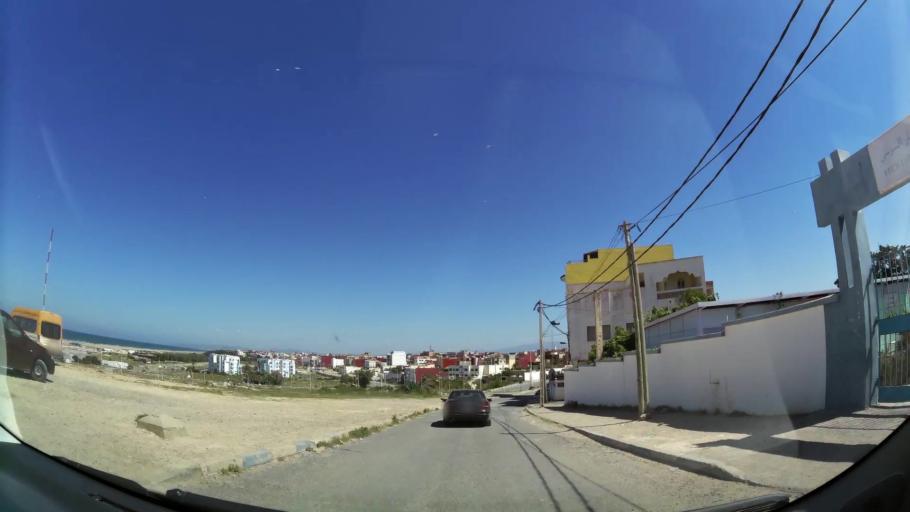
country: MA
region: Oriental
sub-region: Berkane-Taourirt
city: Madagh
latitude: 35.1404
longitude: -2.4260
